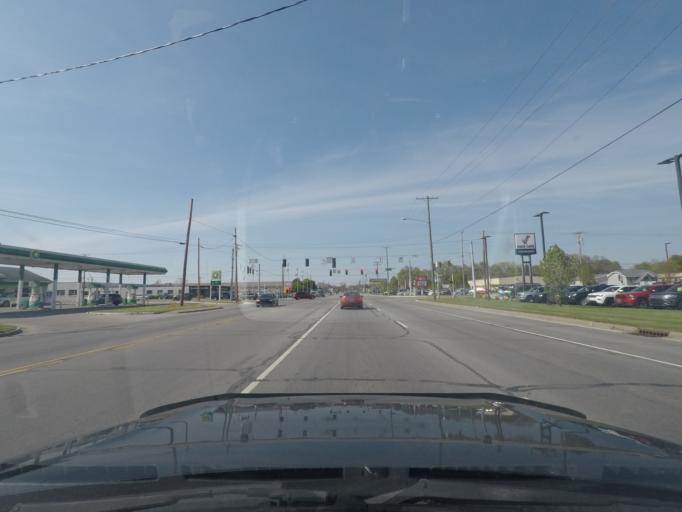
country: US
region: Indiana
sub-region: Elkhart County
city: Elkhart
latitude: 41.6947
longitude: -86.0035
